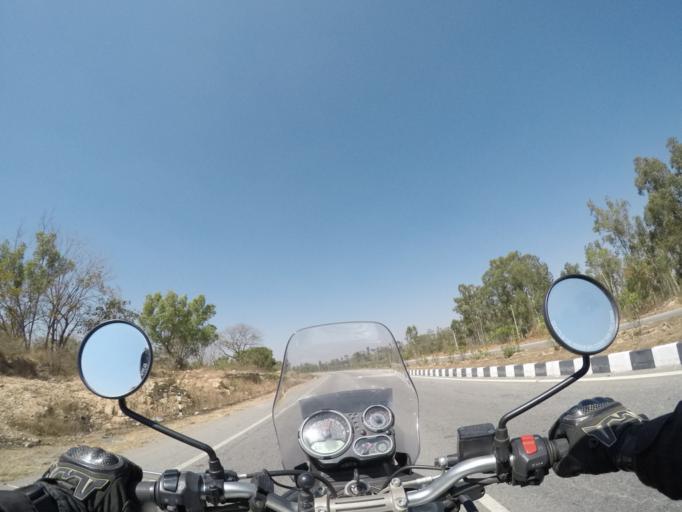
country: IN
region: Karnataka
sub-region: Hassan
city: Hassan
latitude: 12.9934
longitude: 76.1723
